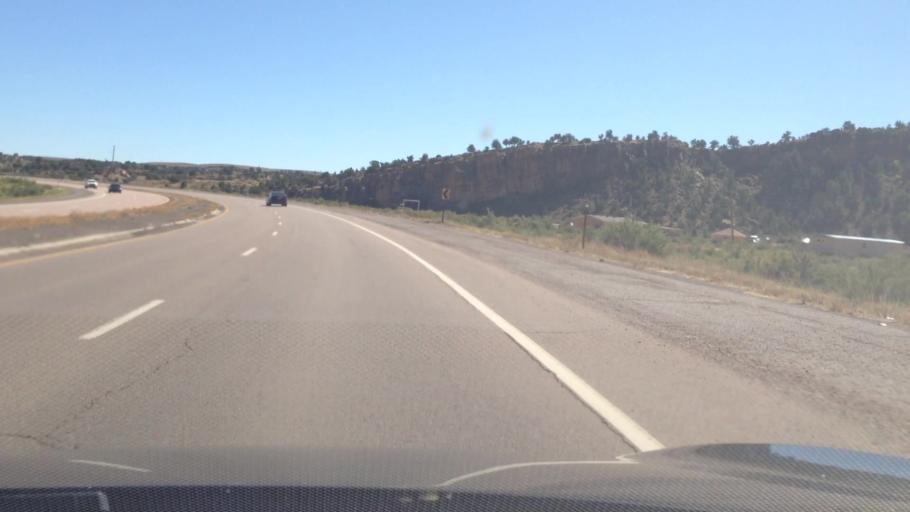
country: US
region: Arizona
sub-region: Apache County
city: Window Rock
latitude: 35.6517
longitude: -109.0389
